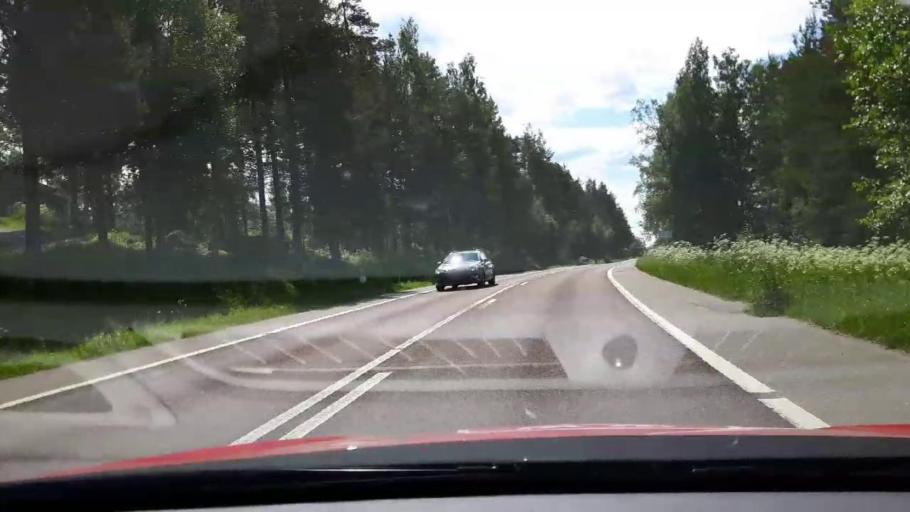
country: SE
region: Jaemtland
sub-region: Harjedalens Kommun
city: Sveg
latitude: 62.1660
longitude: 14.9499
